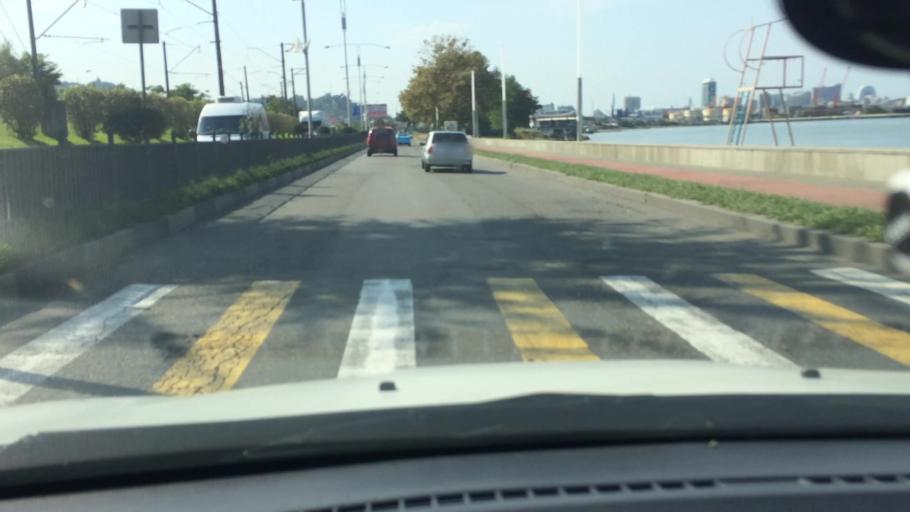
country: GE
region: Ajaria
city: Makhinjauri
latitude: 41.6529
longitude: 41.6703
